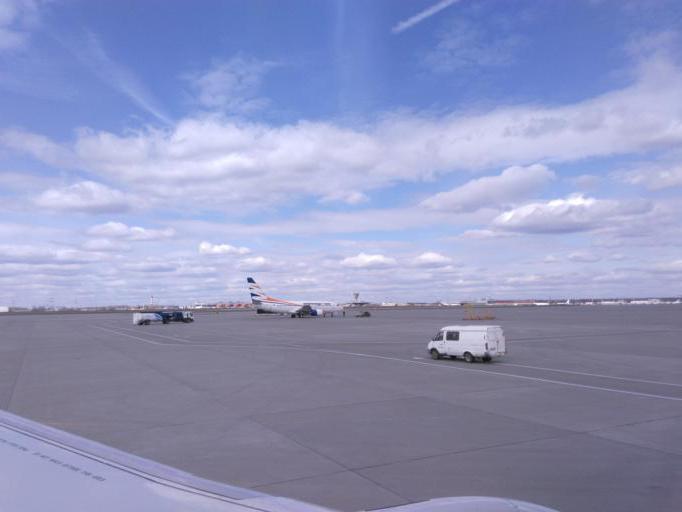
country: RU
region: Moskovskaya
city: Novopodrezkovo
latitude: 55.9651
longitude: 37.4096
